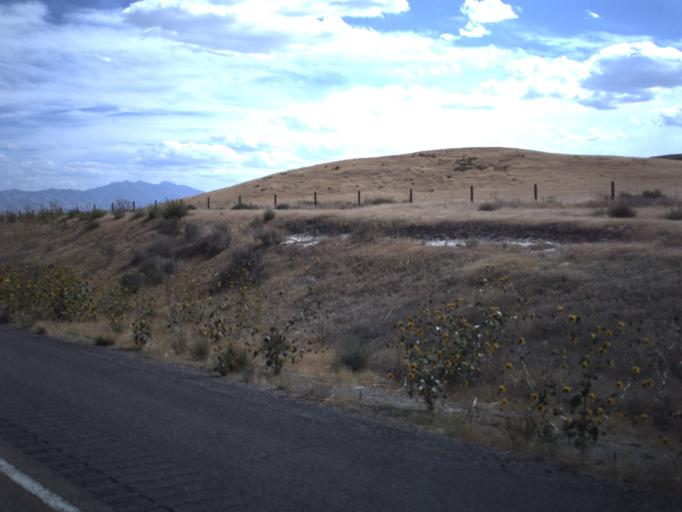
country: US
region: Utah
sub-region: Tooele County
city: Grantsville
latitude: 40.8115
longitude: -112.8708
